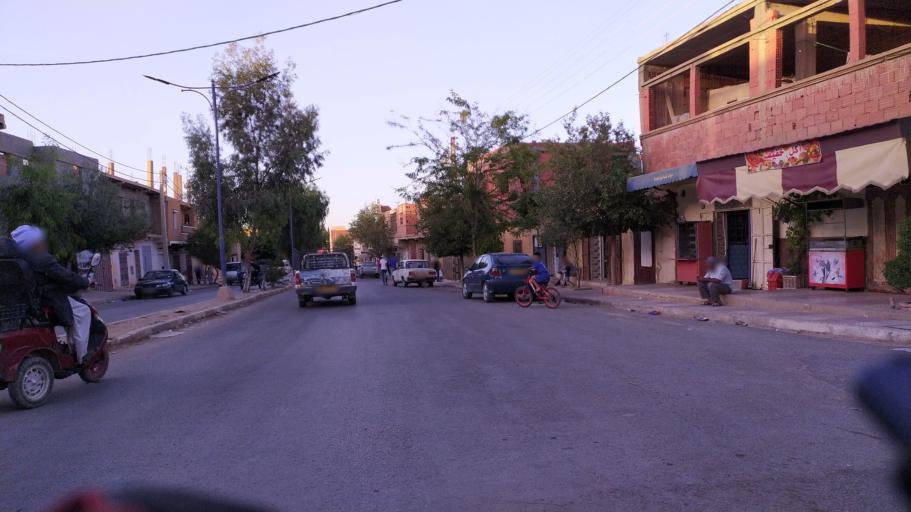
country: DZ
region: Tiaret
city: Frenda
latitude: 34.8929
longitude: 1.2466
